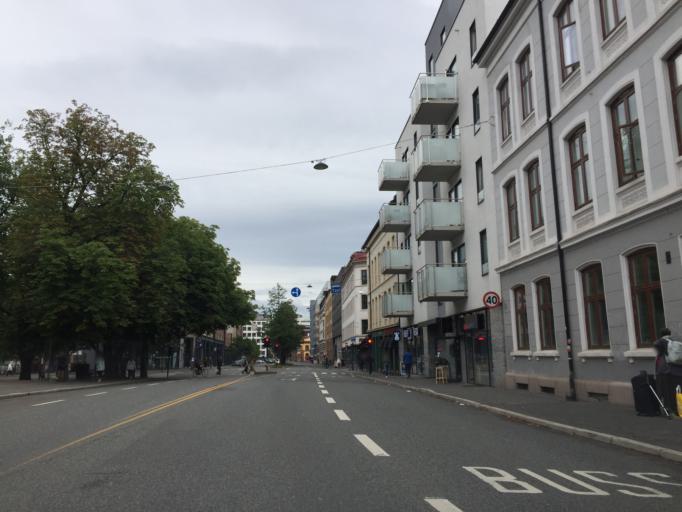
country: NO
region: Oslo
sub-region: Oslo
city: Oslo
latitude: 59.9181
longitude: 10.7535
